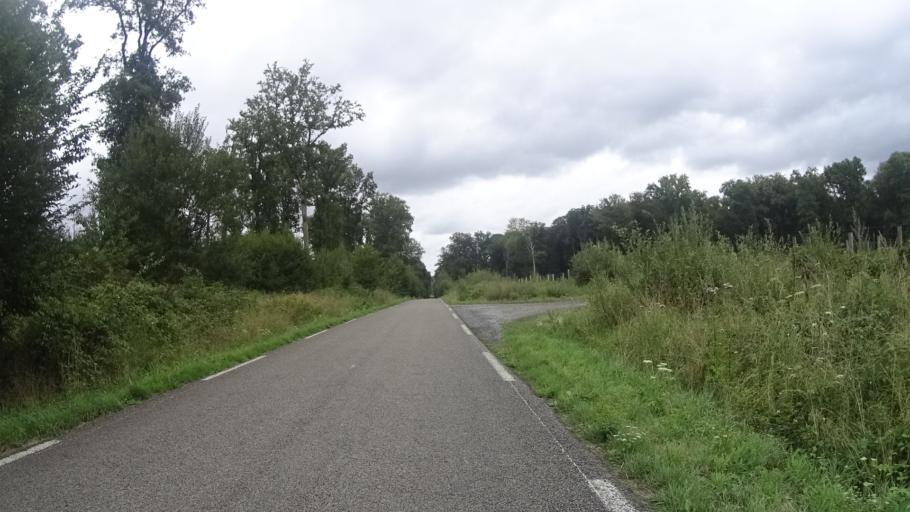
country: FR
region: Nord-Pas-de-Calais
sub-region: Departement du Nord
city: Maroilles
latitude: 50.1642
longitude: 3.7676
